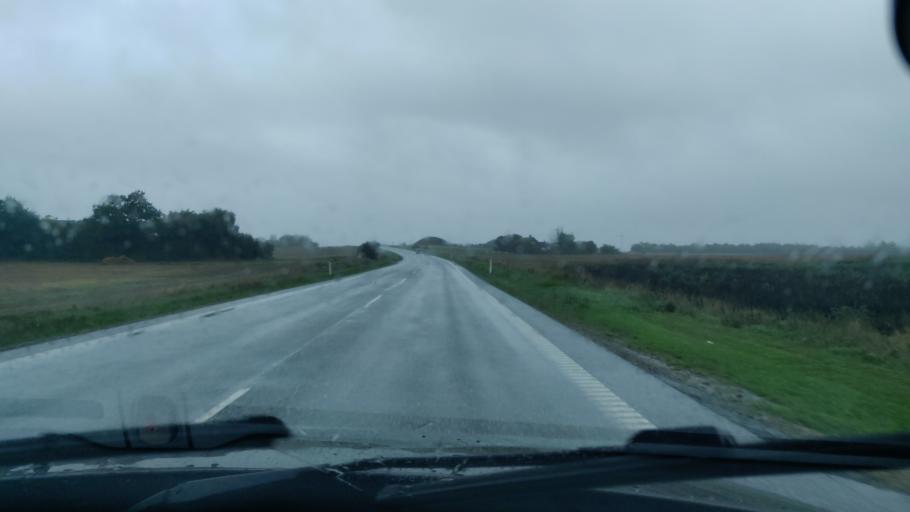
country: DK
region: North Denmark
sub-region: Thisted Kommune
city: Thisted
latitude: 56.8619
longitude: 8.5597
